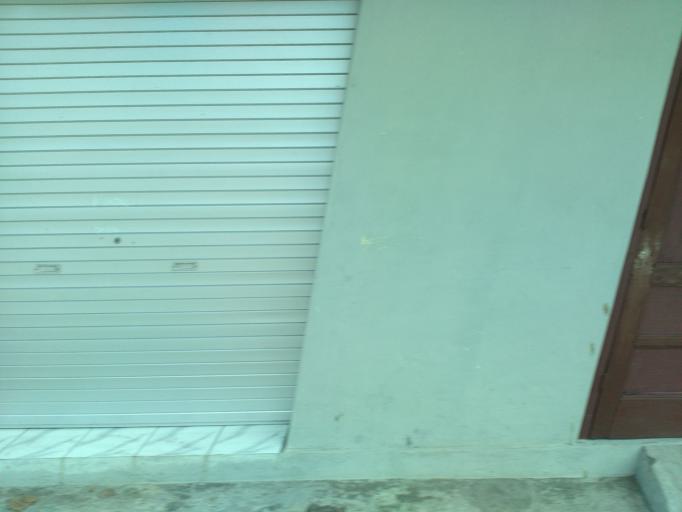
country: ID
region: Central Java
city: Kebonarun
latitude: -7.7177
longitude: 110.5781
